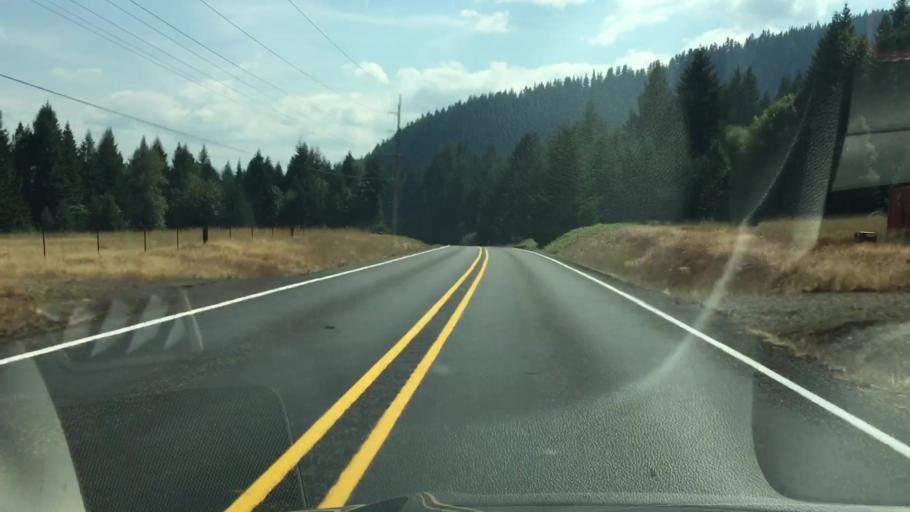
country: US
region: Washington
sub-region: Klickitat County
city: White Salmon
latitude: 45.8821
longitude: -121.5213
